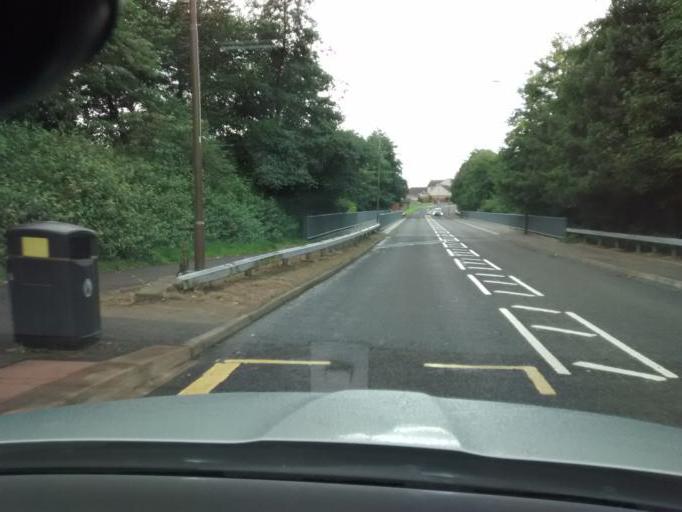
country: GB
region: Scotland
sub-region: West Lothian
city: Livingston
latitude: 55.8903
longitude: -3.5460
